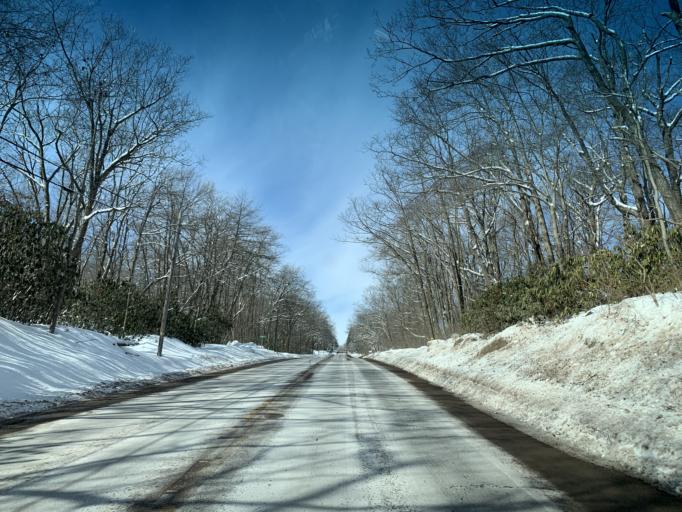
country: US
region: Pennsylvania
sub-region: Somerset County
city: Meyersdale
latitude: 39.7036
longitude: -79.1993
